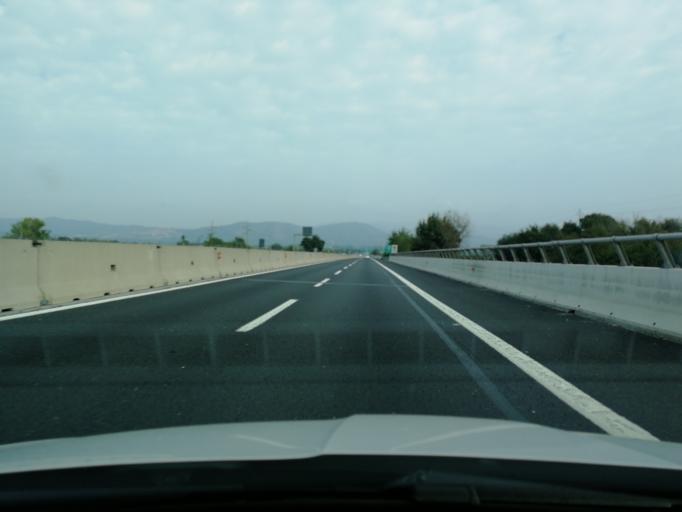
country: IT
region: Latium
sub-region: Citta metropolitana di Roma Capitale
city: Bagni di Tivoli
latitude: 41.9264
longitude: 12.7119
